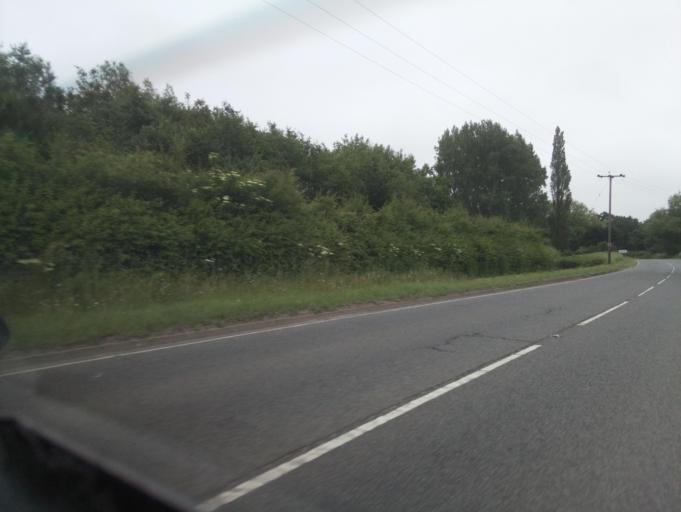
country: GB
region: England
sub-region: Derbyshire
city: Netherseal
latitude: 52.7093
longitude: -1.5561
